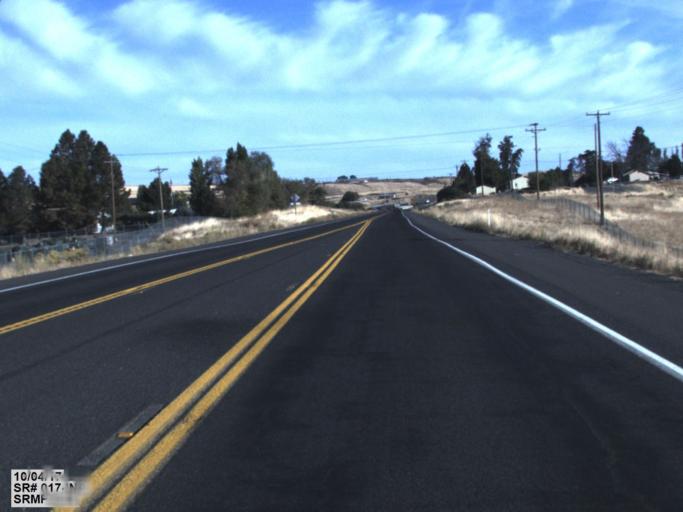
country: US
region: Washington
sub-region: Franklin County
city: Basin City
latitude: 46.5753
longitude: -119.0040
